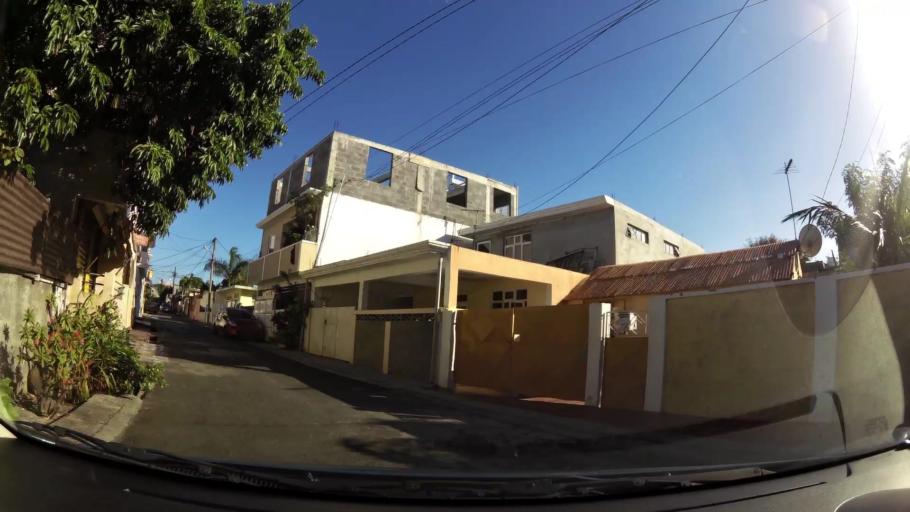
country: MU
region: Port Louis
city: Port Louis
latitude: -20.1690
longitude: 57.4783
